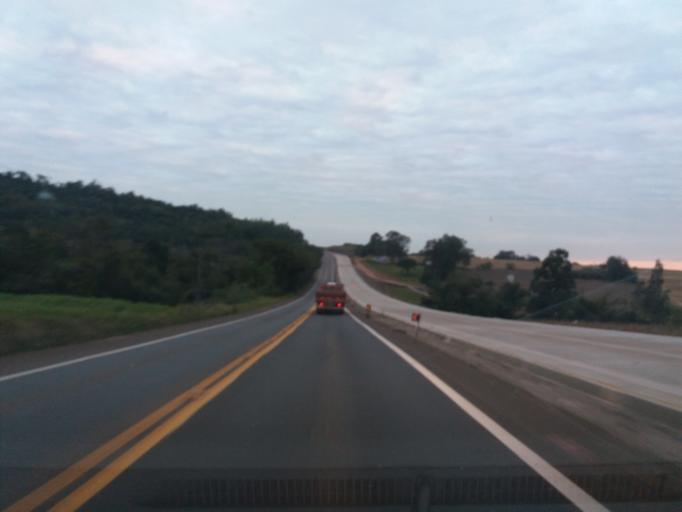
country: BR
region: Parana
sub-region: Realeza
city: Realeza
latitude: -25.3949
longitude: -53.5767
